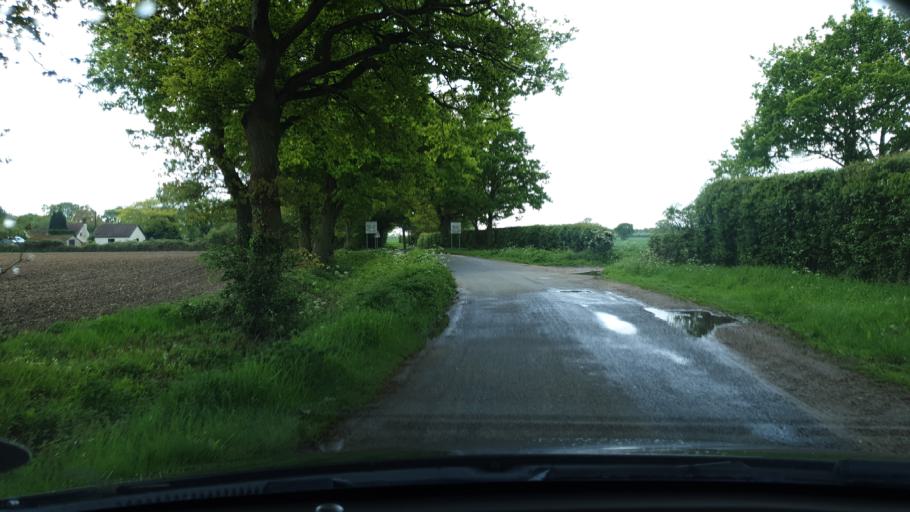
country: GB
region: England
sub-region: Essex
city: Great Bentley
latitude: 51.8803
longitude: 1.0549
